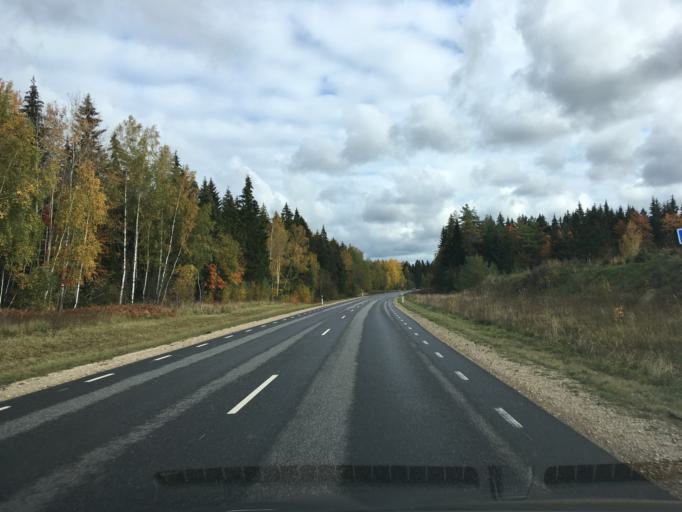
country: EE
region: Harju
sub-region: Anija vald
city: Kehra
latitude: 59.2200
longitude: 25.2400
